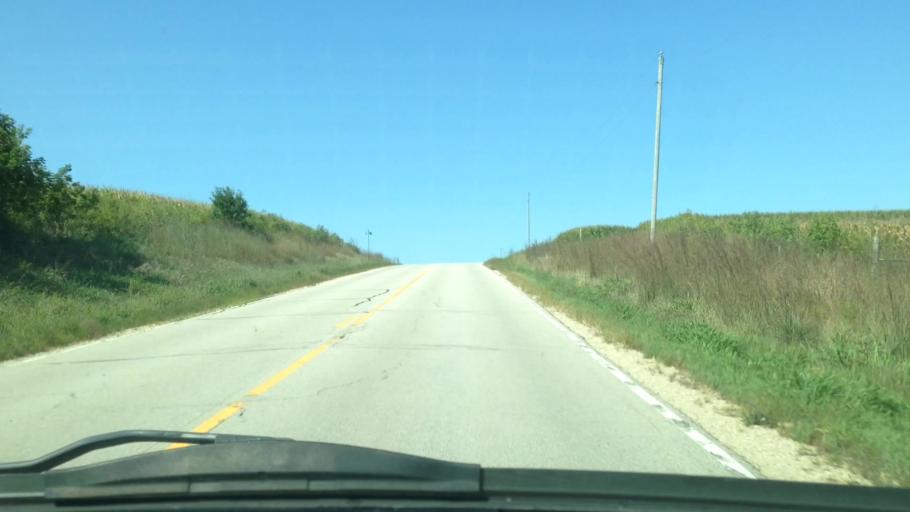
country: US
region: Minnesota
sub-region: Fillmore County
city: Rushford
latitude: 43.6979
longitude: -91.7703
